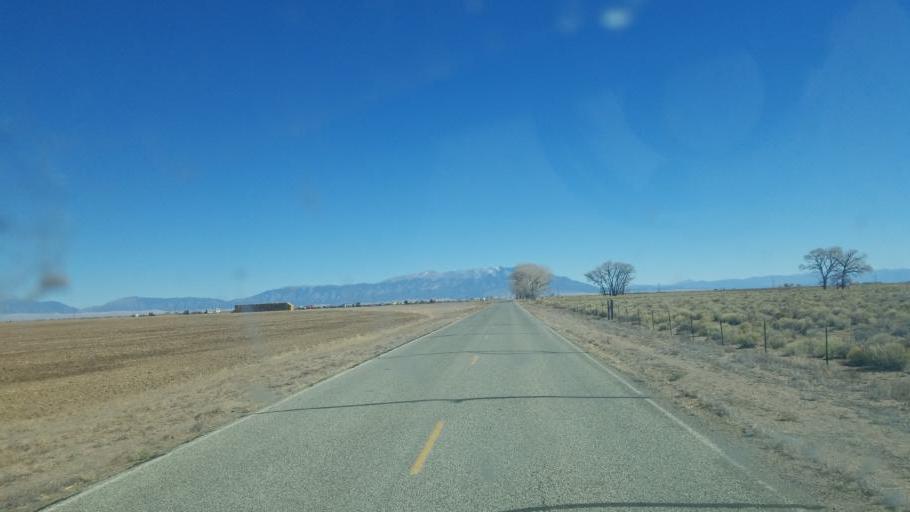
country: US
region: Colorado
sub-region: Alamosa County
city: Alamosa
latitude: 37.5742
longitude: -105.9712
